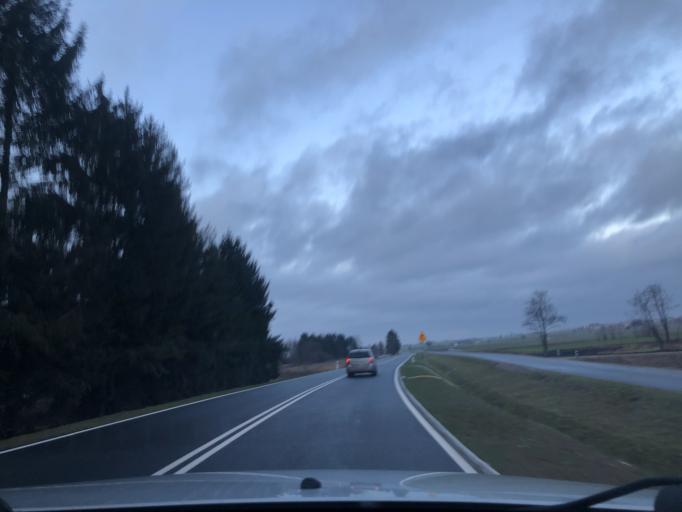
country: PL
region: Podlasie
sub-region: Lomza
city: Lomza
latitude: 53.1285
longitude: 22.0482
